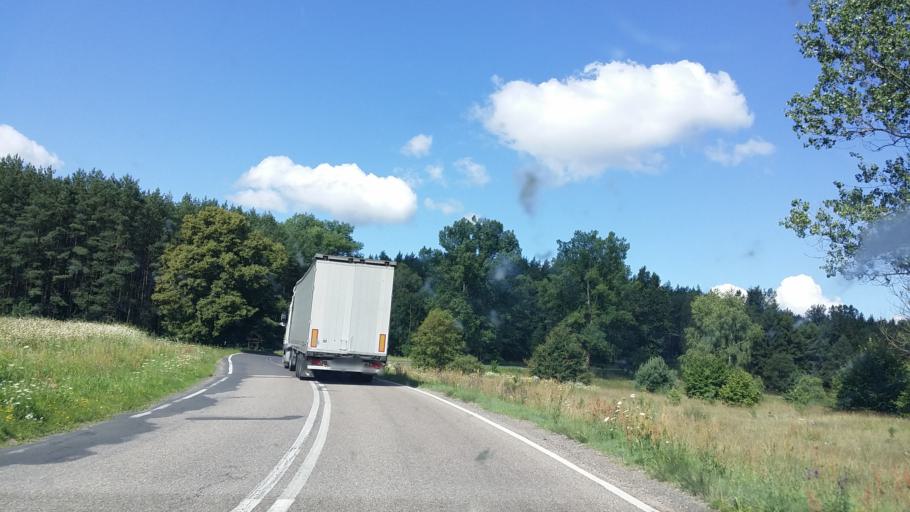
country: PL
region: West Pomeranian Voivodeship
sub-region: Powiat drawski
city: Kalisz Pomorski
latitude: 53.3710
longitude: 15.8766
